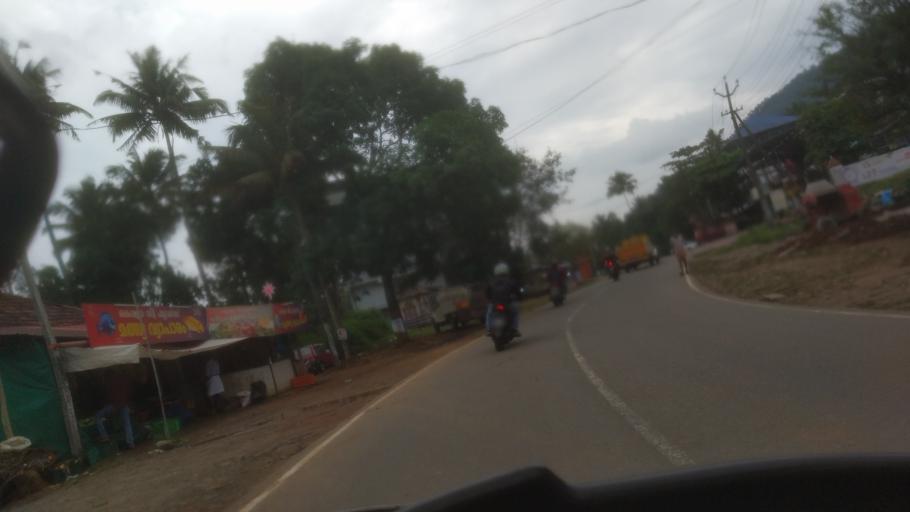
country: IN
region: Kerala
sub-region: Idukki
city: Munnar
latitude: 9.9953
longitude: 76.9765
